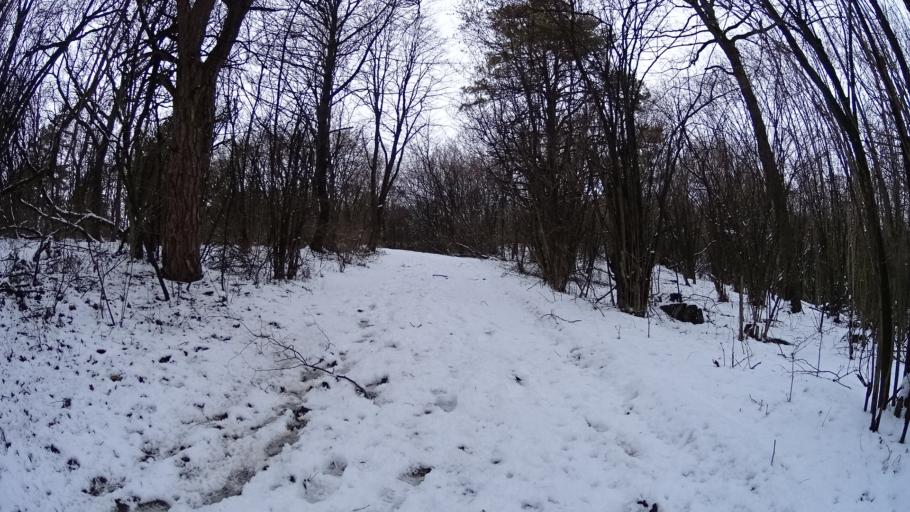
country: AT
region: Lower Austria
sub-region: Politischer Bezirk Korneuburg
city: Niederhollabrunn
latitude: 48.4260
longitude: 16.2906
